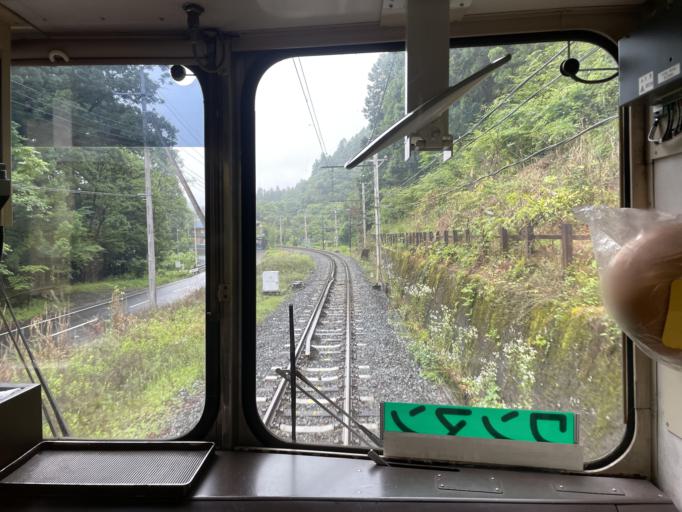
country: JP
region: Saitama
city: Chichibu
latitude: 35.9559
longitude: 139.0058
